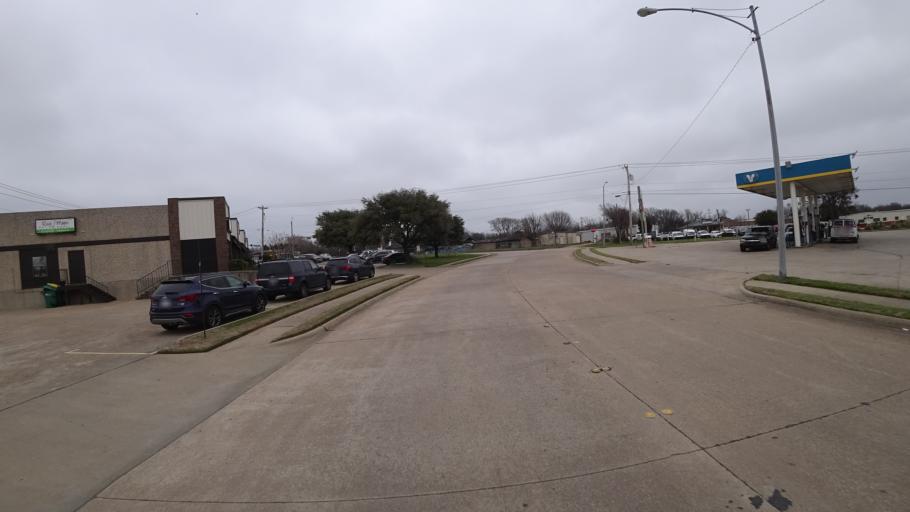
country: US
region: Texas
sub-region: Denton County
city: Lewisville
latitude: 33.0569
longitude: -97.0012
